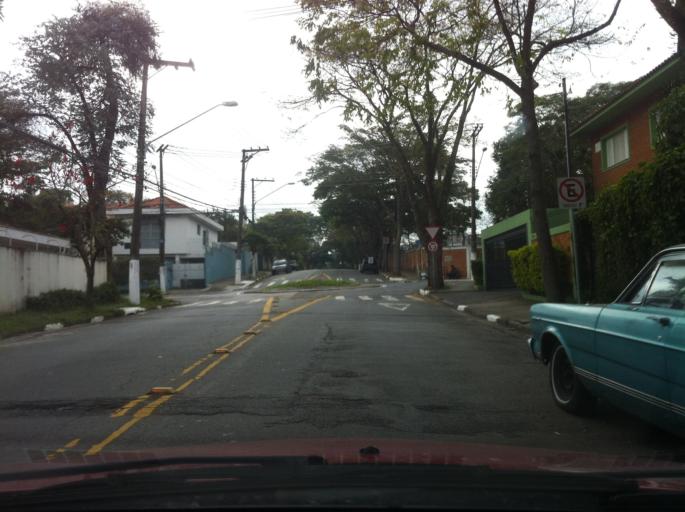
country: BR
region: Sao Paulo
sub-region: Diadema
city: Diadema
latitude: -23.6404
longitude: -46.6943
